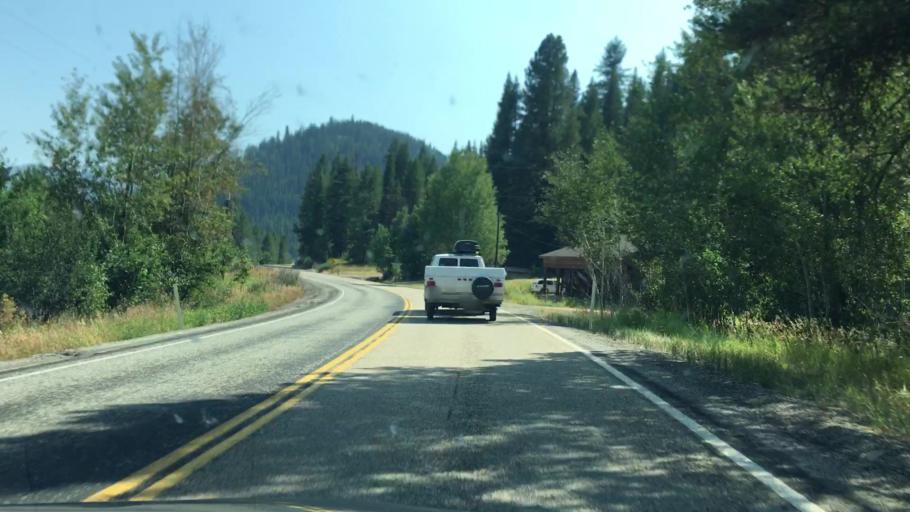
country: US
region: Idaho
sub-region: Valley County
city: Cascade
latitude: 44.3080
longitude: -116.0875
